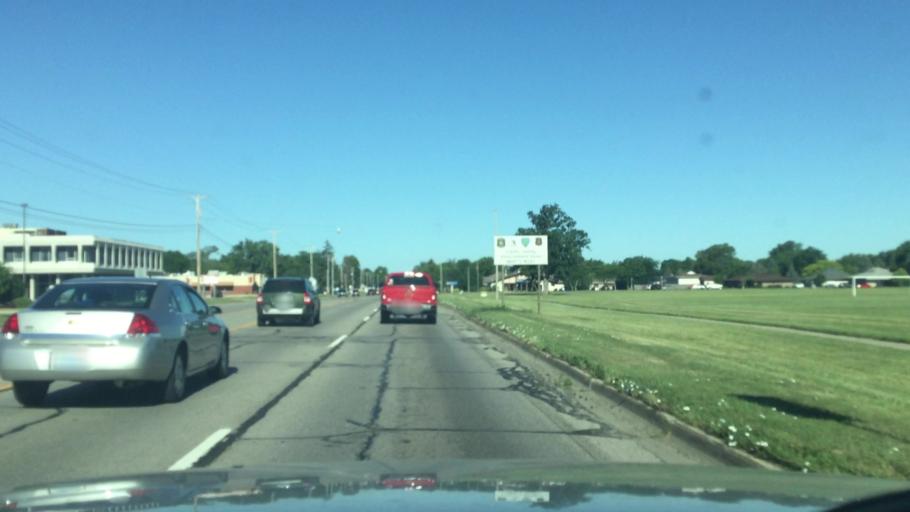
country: US
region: Michigan
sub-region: Saginaw County
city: Shields
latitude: 43.4154
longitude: -84.0163
